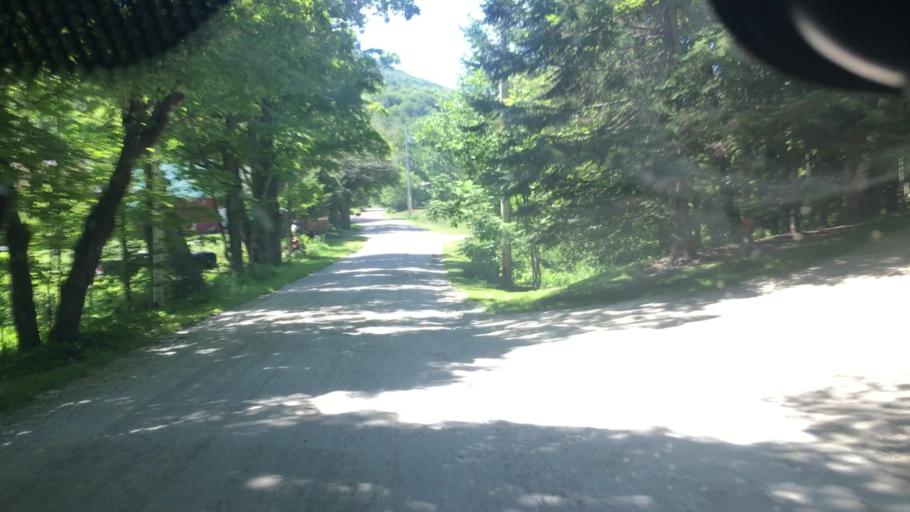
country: US
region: Vermont
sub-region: Windsor County
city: Chester
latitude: 43.4306
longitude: -72.7135
